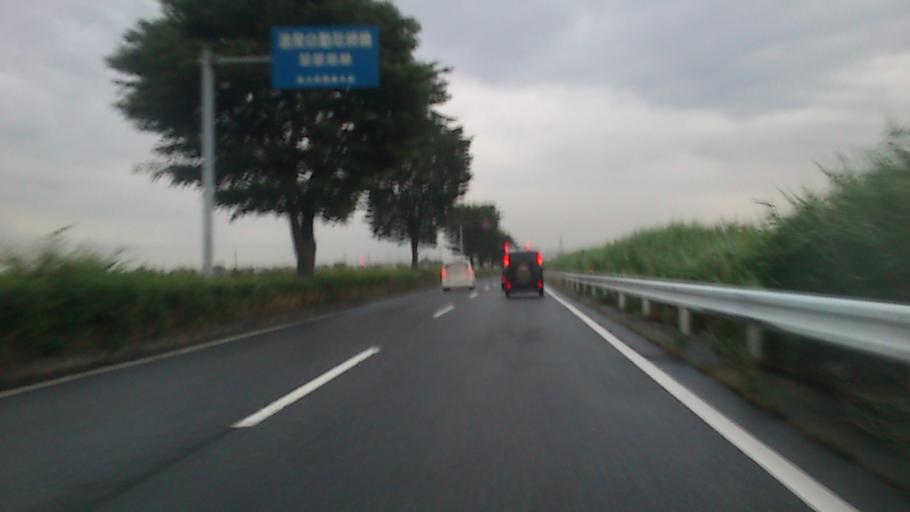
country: JP
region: Saitama
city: Kumagaya
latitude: 36.1482
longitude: 139.4235
